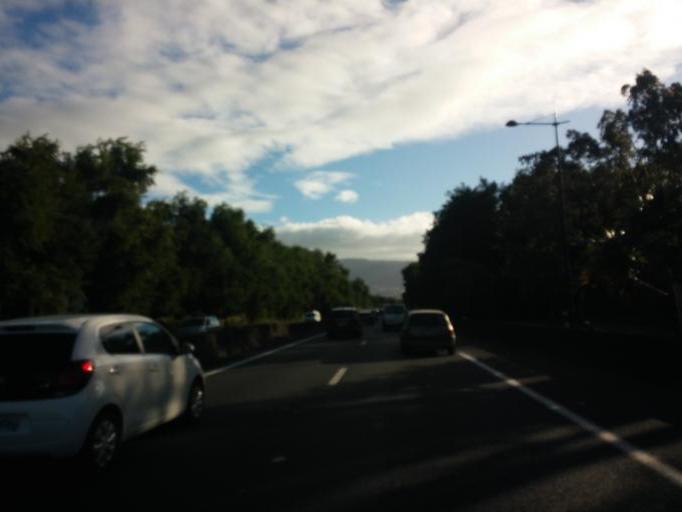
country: RE
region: Reunion
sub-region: Reunion
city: Saint-Denis
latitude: -20.8859
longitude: 55.4955
